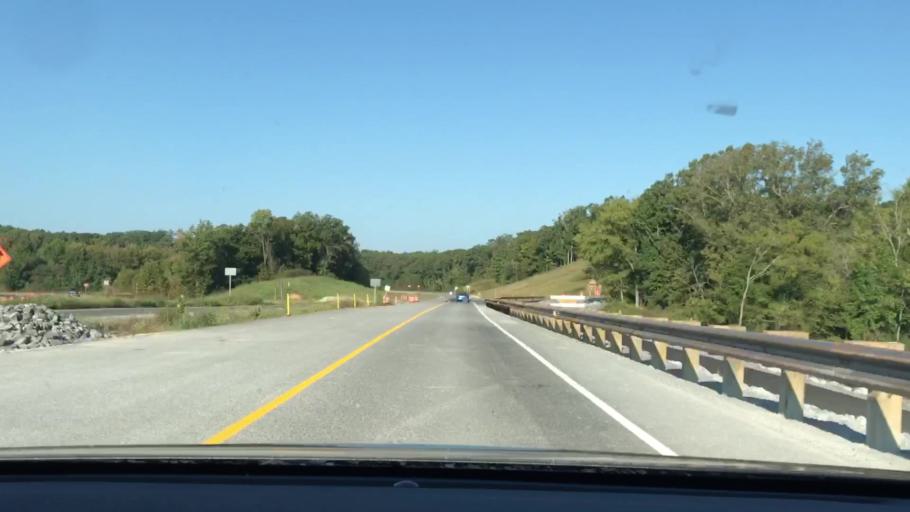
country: US
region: Kentucky
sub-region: Trigg County
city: Cadiz
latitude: 36.8007
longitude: -87.9849
